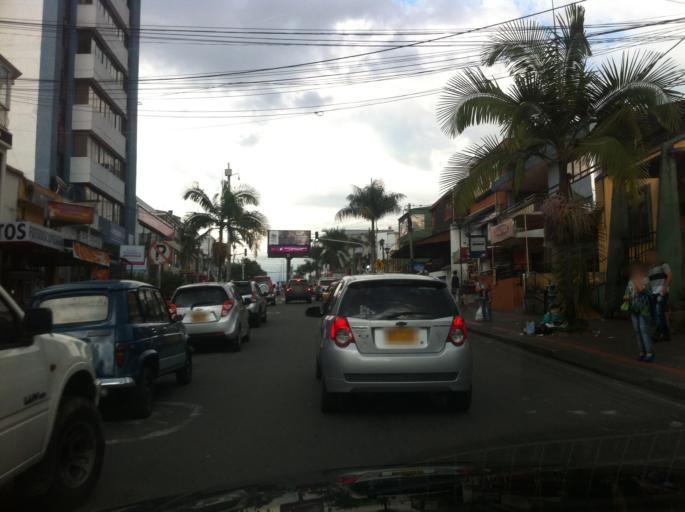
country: CO
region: Quindio
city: Armenia
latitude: 4.5378
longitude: -75.6676
